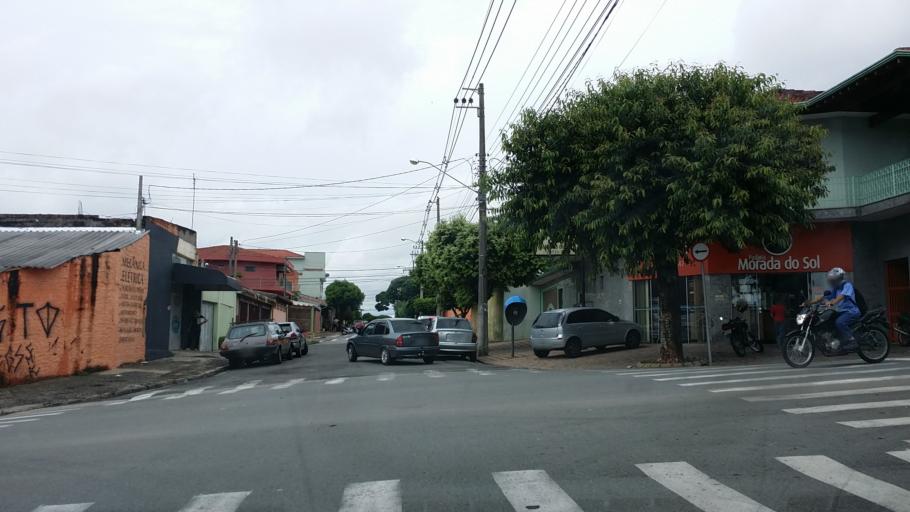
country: BR
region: Sao Paulo
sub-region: Indaiatuba
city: Indaiatuba
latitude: -23.1235
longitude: -47.2303
